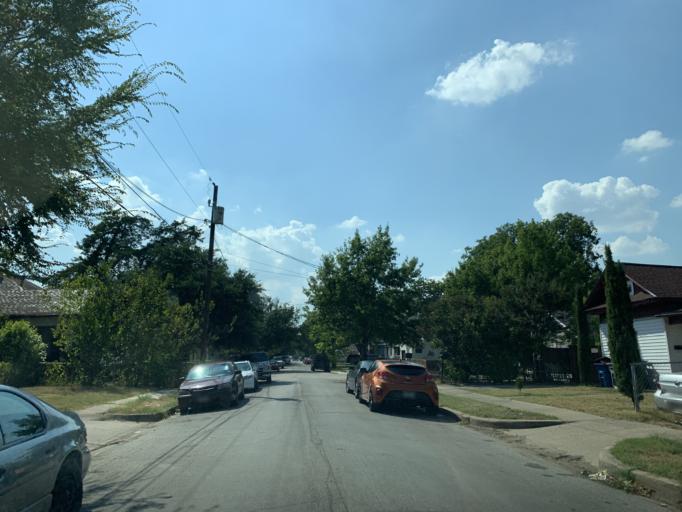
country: US
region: Texas
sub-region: Dallas County
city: Dallas
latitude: 32.7473
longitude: -96.8334
